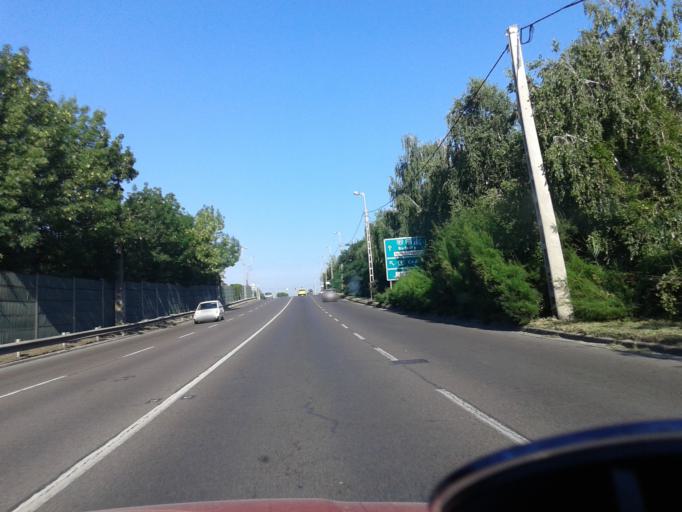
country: HU
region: Budapest
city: Budapest XI. keruelet
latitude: 47.4521
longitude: 19.0125
